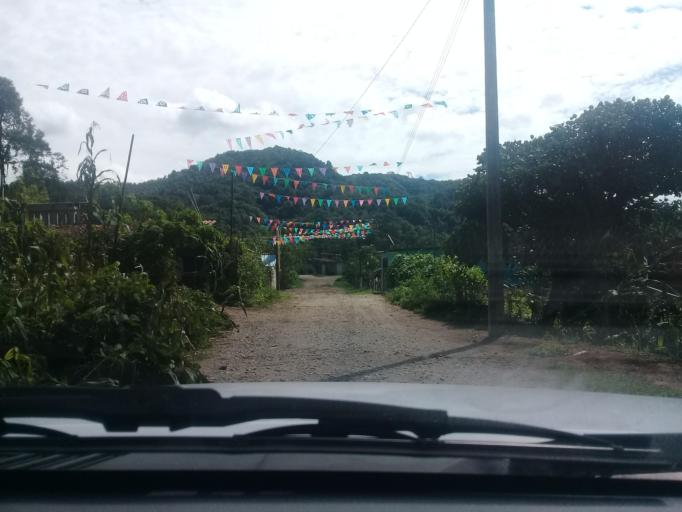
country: MX
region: Veracruz
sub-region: Tlalnelhuayocan
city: Otilpan
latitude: 19.5660
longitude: -96.9826
